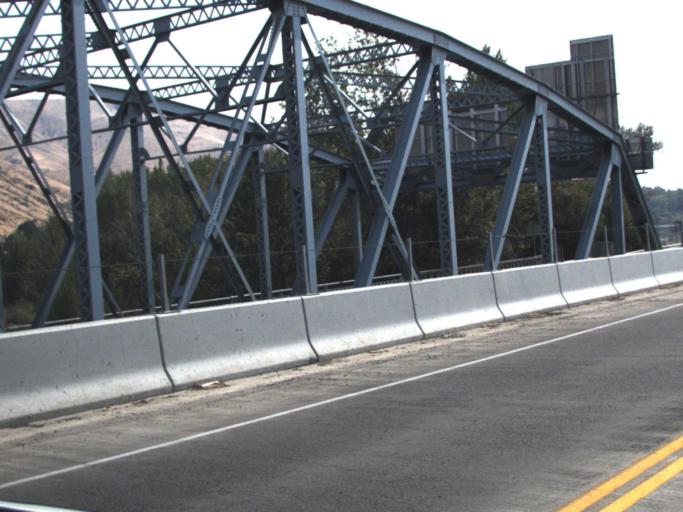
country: US
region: Washington
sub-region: Yakima County
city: Selah
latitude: 46.6300
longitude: -120.5155
